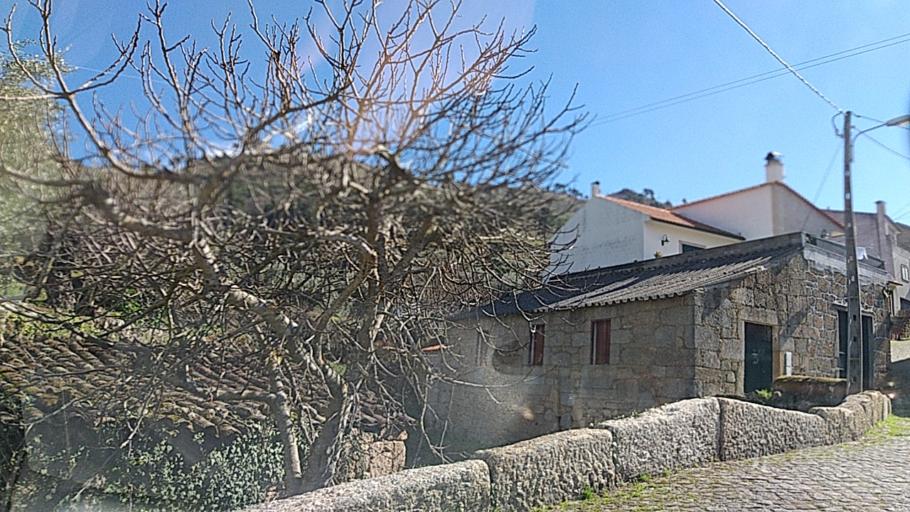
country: PT
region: Guarda
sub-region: Guarda
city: Guarda
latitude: 40.5875
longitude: -7.2875
